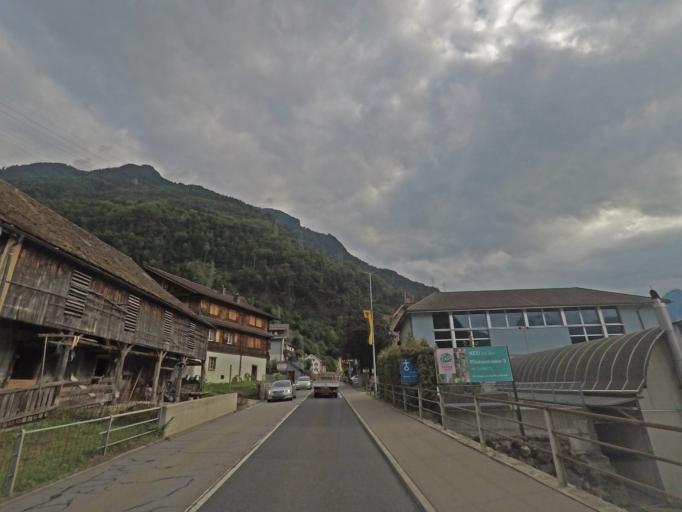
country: CH
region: Uri
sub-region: Uri
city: Bauen
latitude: 46.9513
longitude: 8.6216
